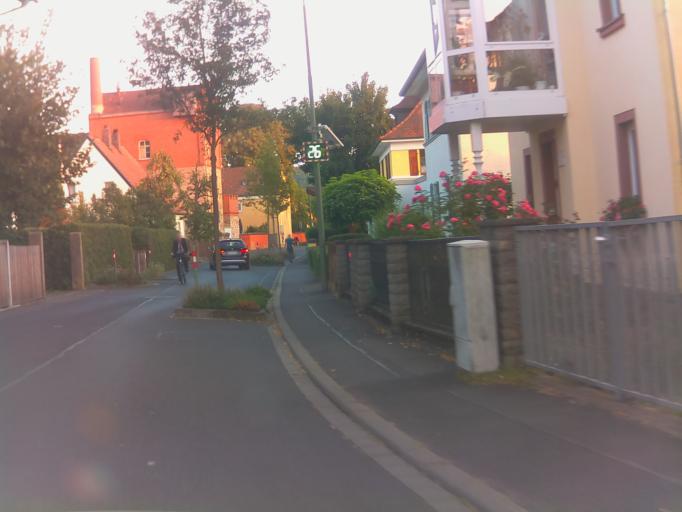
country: DE
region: Bavaria
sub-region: Regierungsbezirk Unterfranken
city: Hammelburg
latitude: 50.1177
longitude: 9.8925
